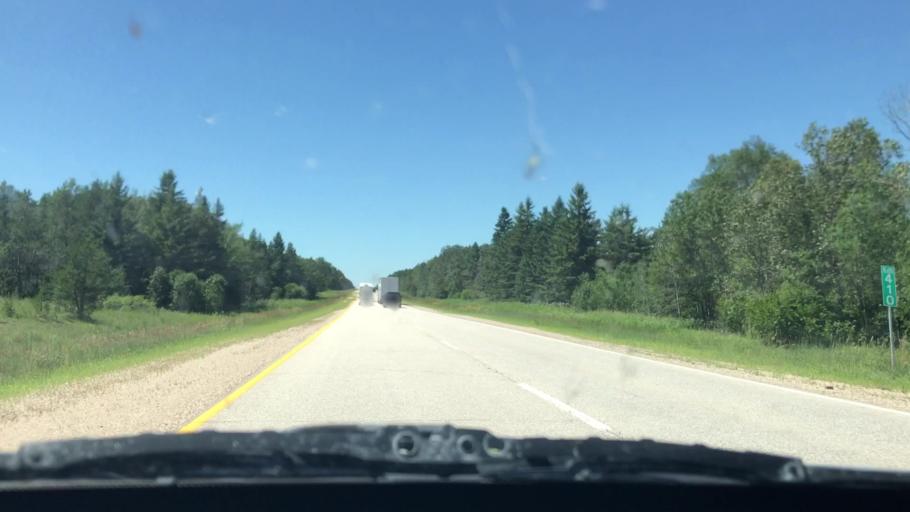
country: CA
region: Manitoba
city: La Broquerie
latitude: 49.6572
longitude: -96.1905
